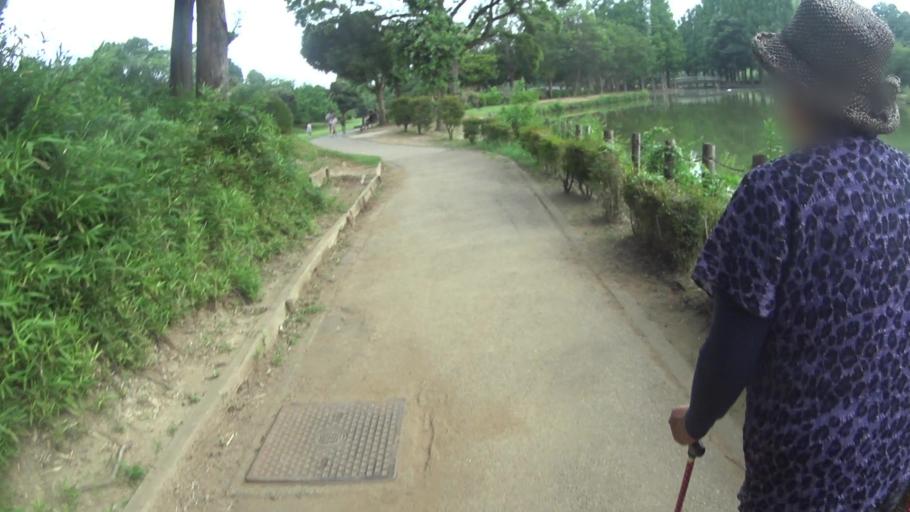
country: JP
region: Saitama
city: Okegawa
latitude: 35.9577
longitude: 139.5473
